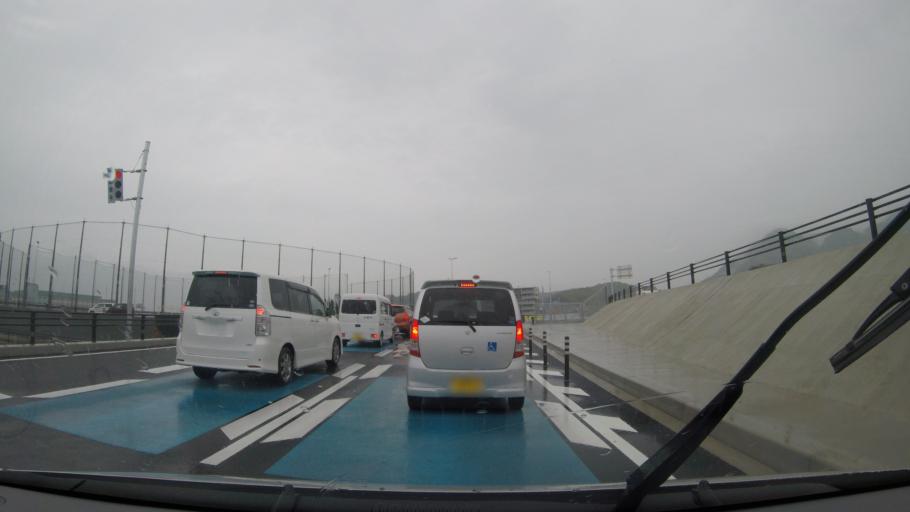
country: JP
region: Fukuoka
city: Shingu
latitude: 33.6695
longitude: 130.4499
